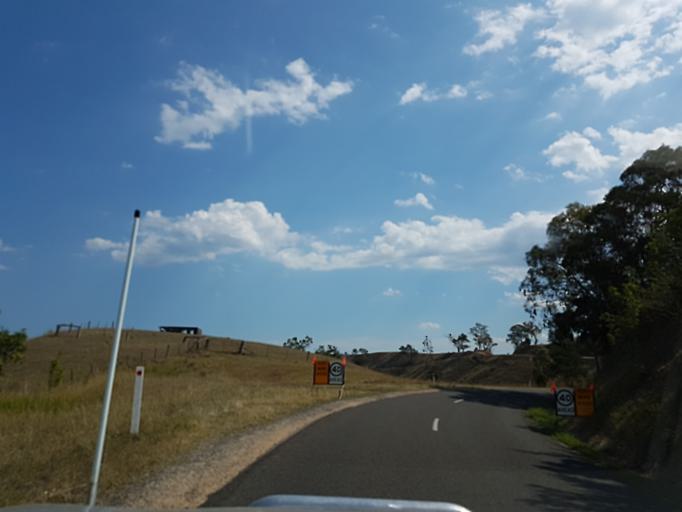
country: AU
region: Victoria
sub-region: East Gippsland
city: Lakes Entrance
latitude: -37.4991
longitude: 148.1937
